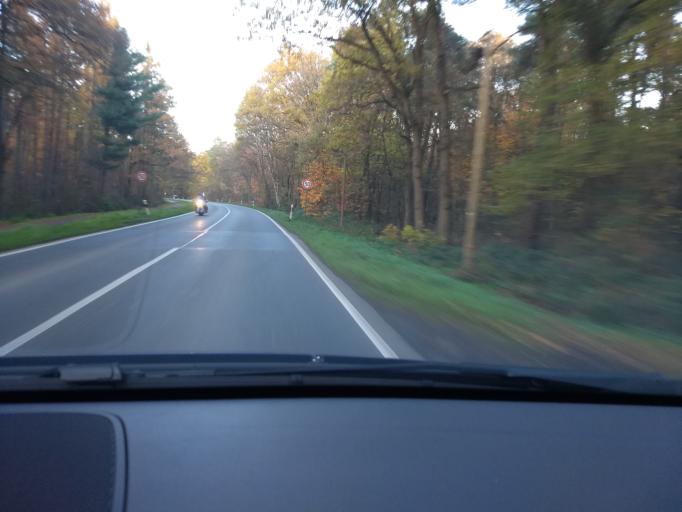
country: DE
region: North Rhine-Westphalia
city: Marl
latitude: 51.7267
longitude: 7.0891
